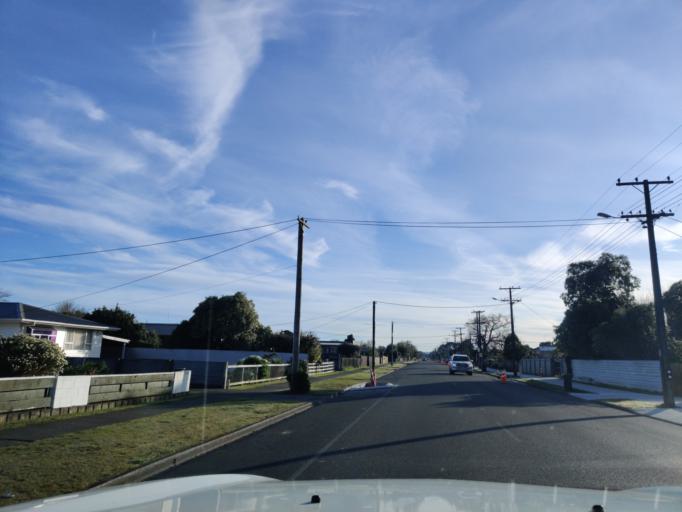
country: NZ
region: Manawatu-Wanganui
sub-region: Palmerston North City
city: Palmerston North
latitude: -40.2889
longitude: 175.7583
